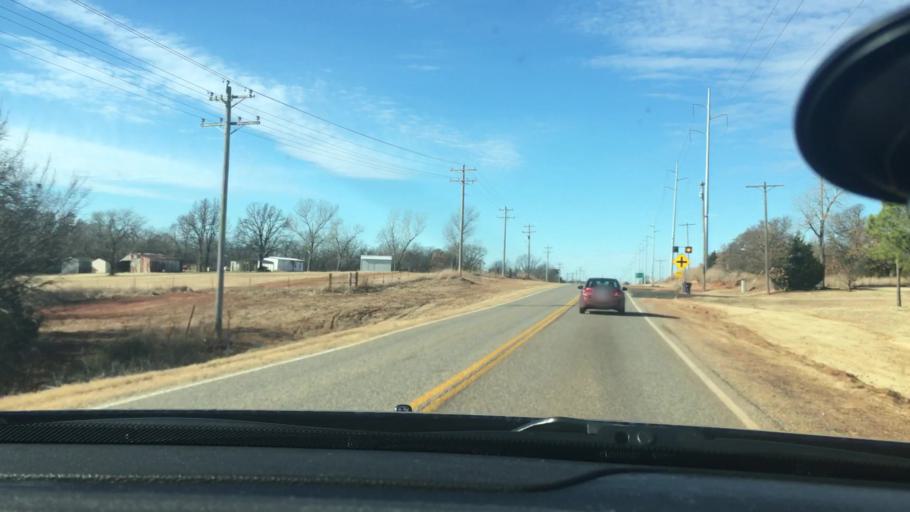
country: US
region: Oklahoma
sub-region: Cleveland County
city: Lexington
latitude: 35.0151
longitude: -97.1908
